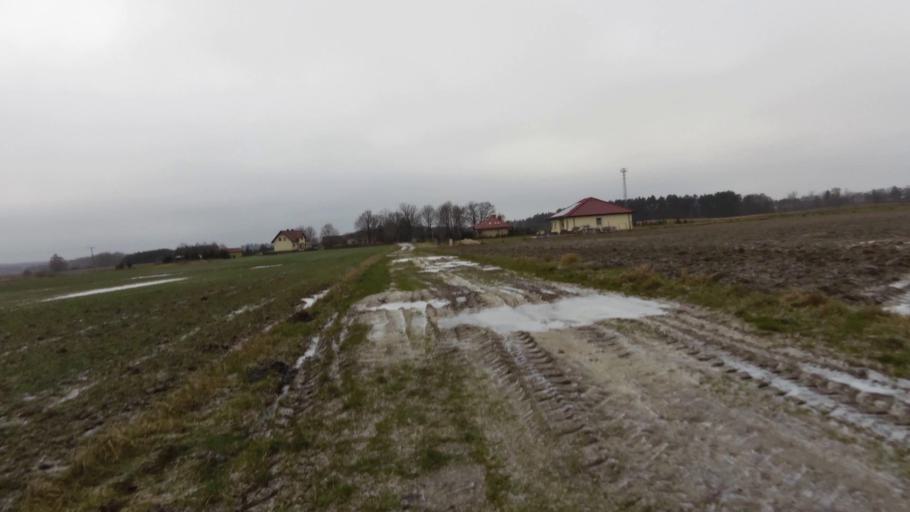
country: PL
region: West Pomeranian Voivodeship
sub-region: Powiat szczecinecki
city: Szczecinek
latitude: 53.6416
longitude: 16.6180
